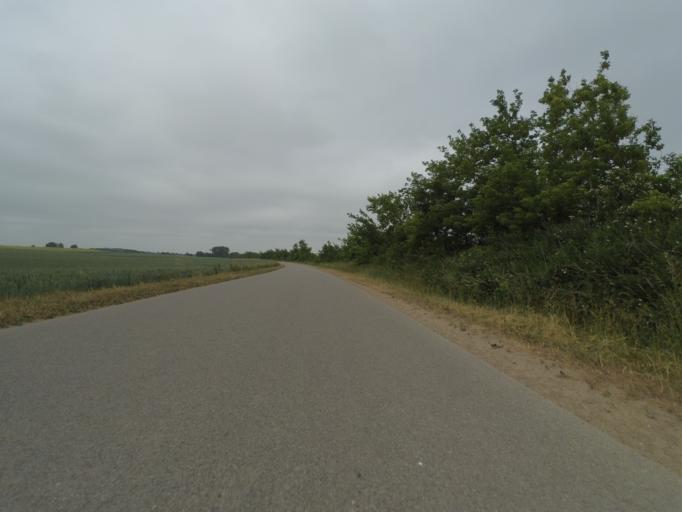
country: DE
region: Mecklenburg-Vorpommern
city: Goldberg
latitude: 53.5555
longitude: 12.0776
